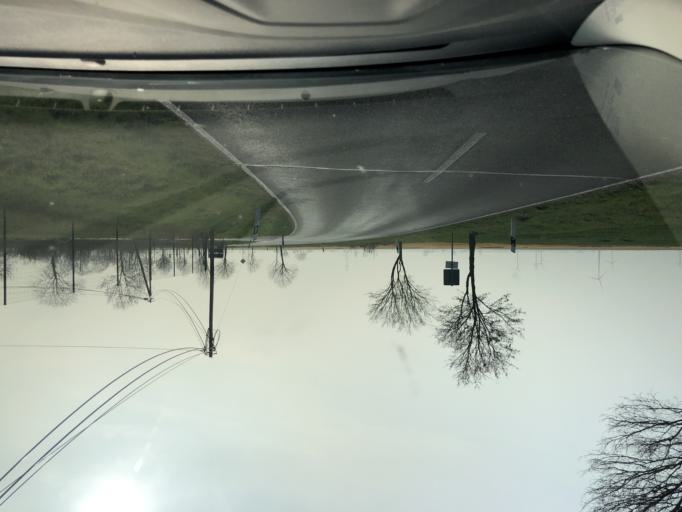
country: DE
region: Saxony-Anhalt
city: Zorbig
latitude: 51.5995
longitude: 12.1165
